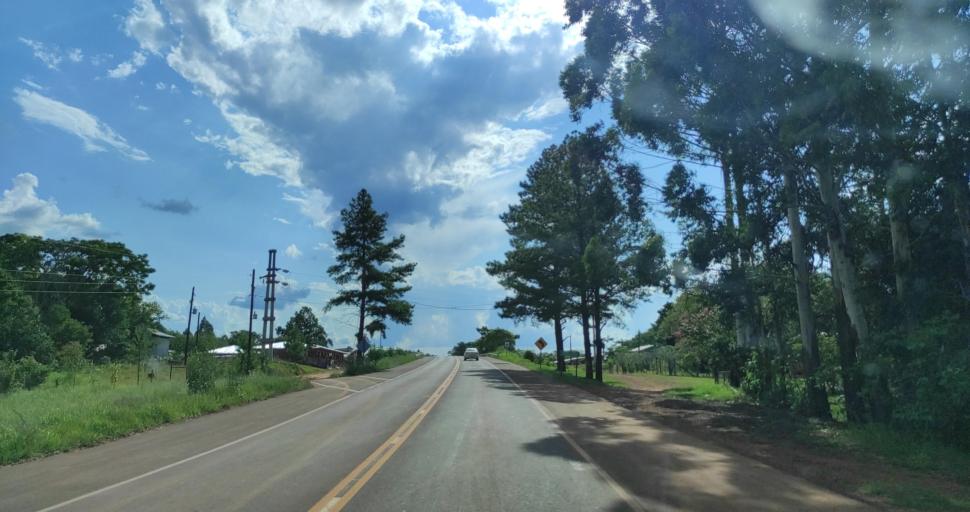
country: AR
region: Misiones
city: Bernardo de Irigoyen
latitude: -26.2954
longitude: -53.7880
